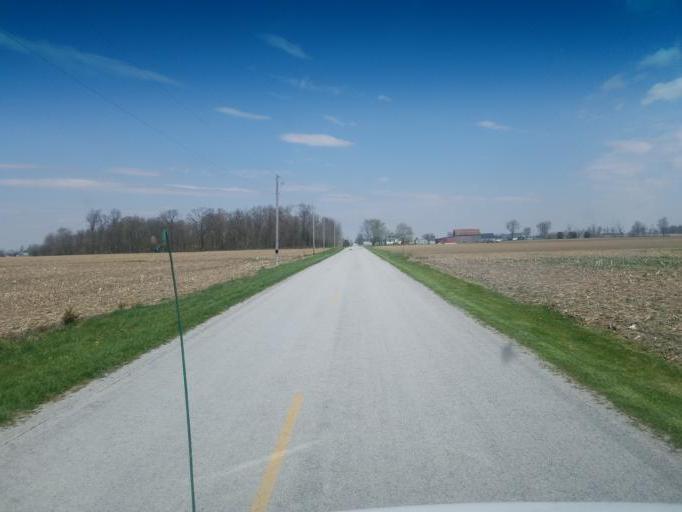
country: US
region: Ohio
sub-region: Hardin County
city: Forest
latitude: 40.7409
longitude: -83.5378
